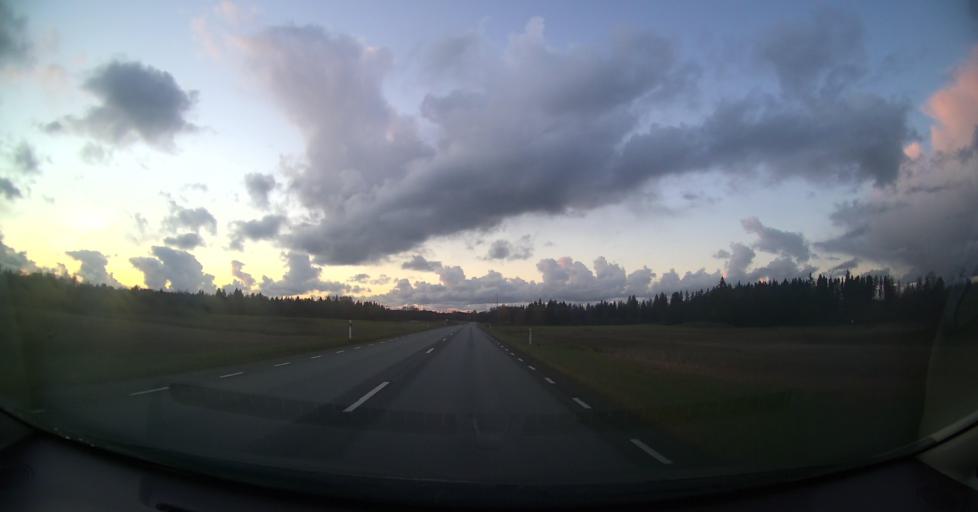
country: EE
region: Harju
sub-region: Raasiku vald
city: Raasiku
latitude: 59.4085
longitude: 25.2627
